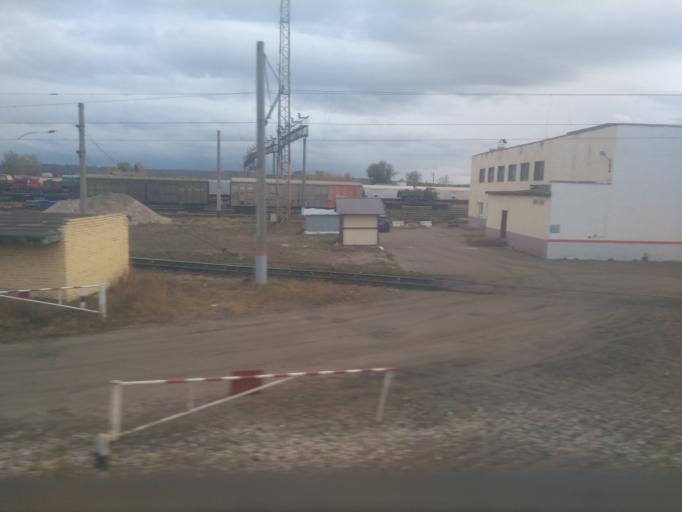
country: RU
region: Tatarstan
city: Osinovo
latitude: 55.8171
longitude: 48.9006
